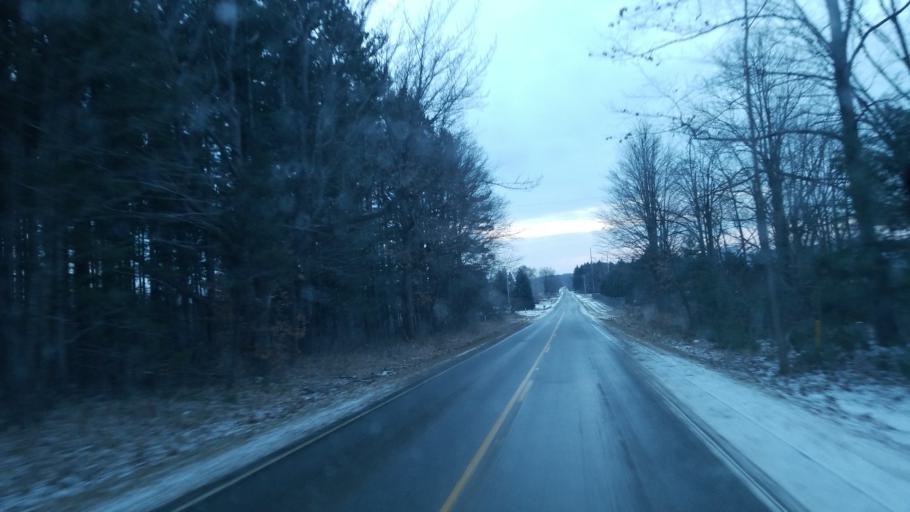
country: US
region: Michigan
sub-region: Osceola County
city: Reed City
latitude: 43.8413
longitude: -85.4242
